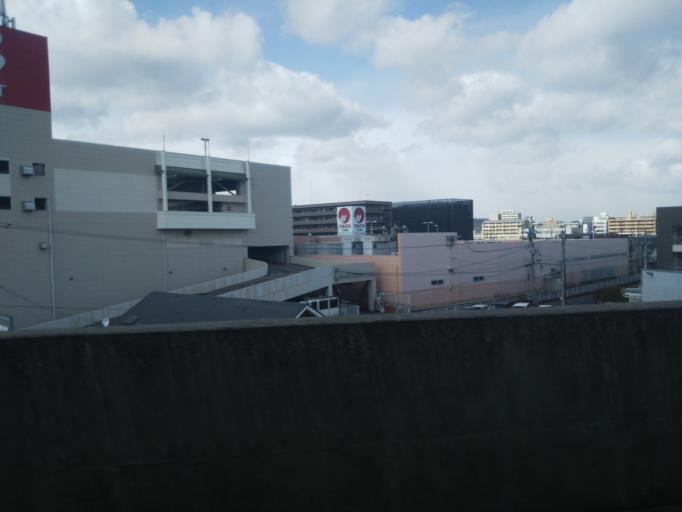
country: JP
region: Okayama
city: Okayama-shi
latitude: 34.6344
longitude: 133.9028
